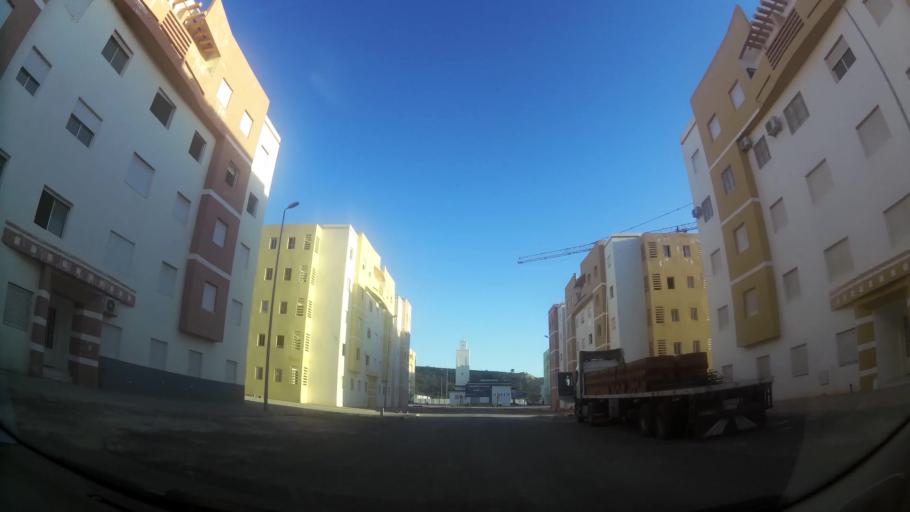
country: MA
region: Oriental
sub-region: Berkane-Taourirt
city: Madagh
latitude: 35.0765
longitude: -2.2378
